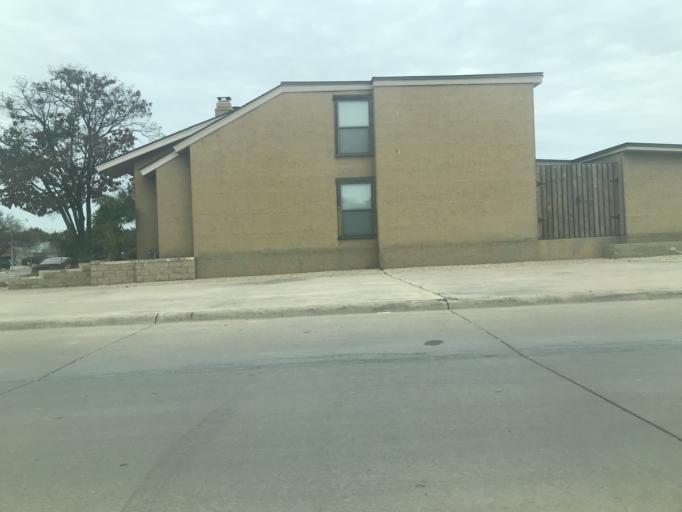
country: US
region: Texas
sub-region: Tom Green County
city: San Angelo
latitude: 31.4225
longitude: -100.4747
